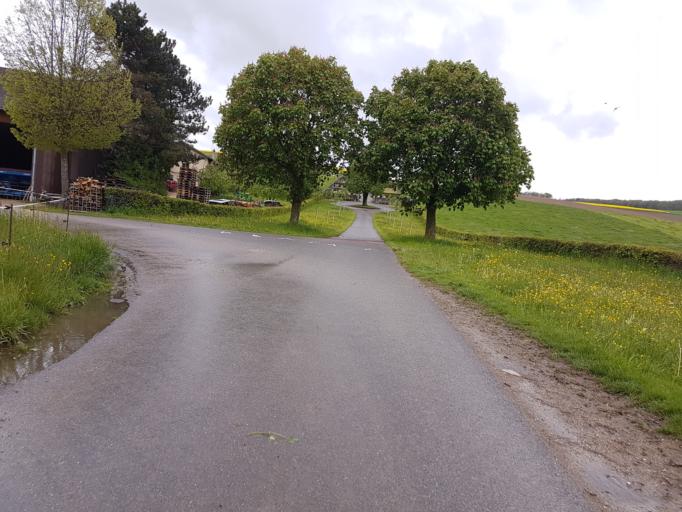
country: CH
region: Vaud
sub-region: Morges District
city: Orny
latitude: 46.6483
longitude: 6.5287
